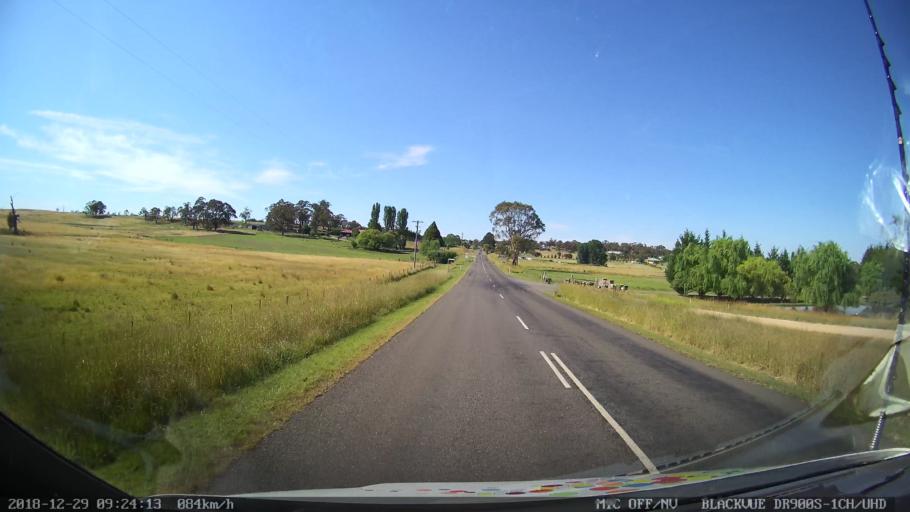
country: AU
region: New South Wales
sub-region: Upper Lachlan Shire
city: Crookwell
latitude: -34.5336
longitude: 149.3948
